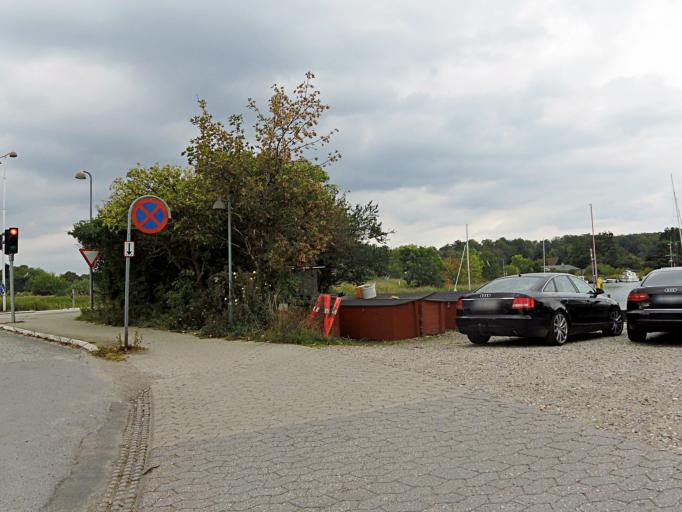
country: DK
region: Capital Region
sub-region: Fredensborg Kommune
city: Niva
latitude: 55.9386
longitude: 12.5240
